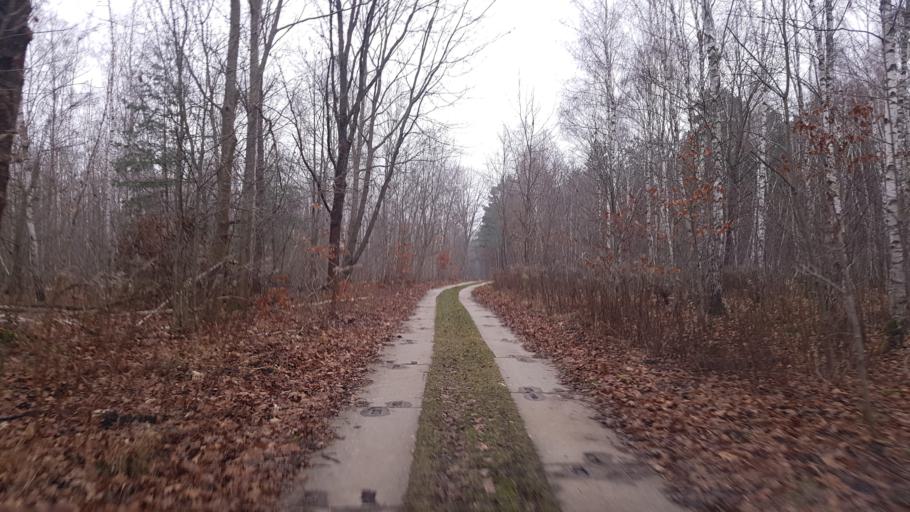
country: DE
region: Brandenburg
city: Plessa
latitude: 51.4945
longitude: 13.6378
